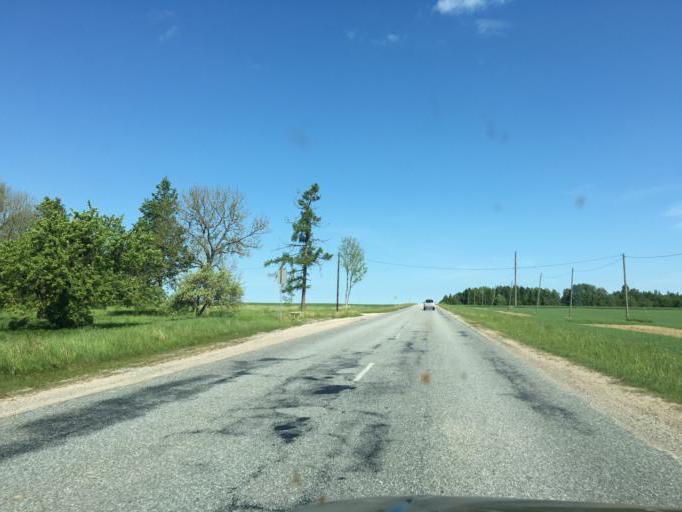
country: LV
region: Talsu Rajons
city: Valdemarpils
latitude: 57.3574
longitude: 22.4935
